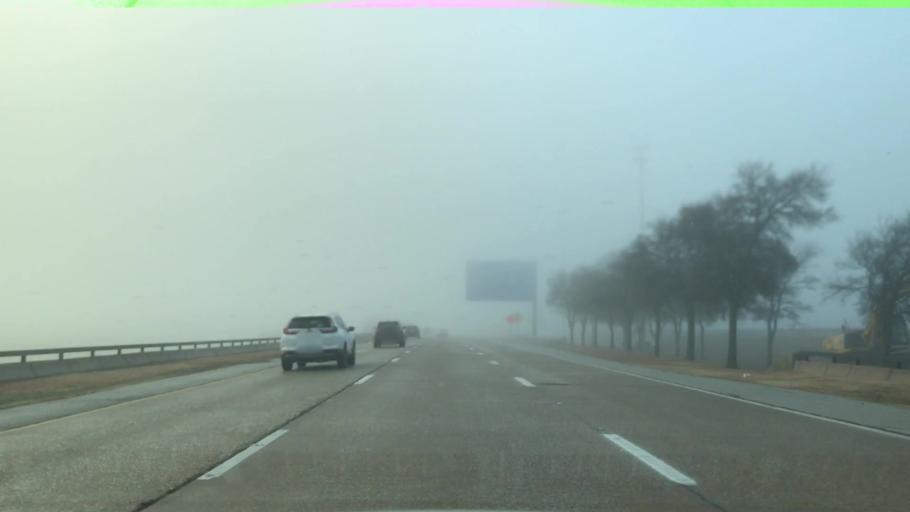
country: US
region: Texas
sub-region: Tarrant County
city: Grapevine
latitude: 32.9166
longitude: -97.0410
